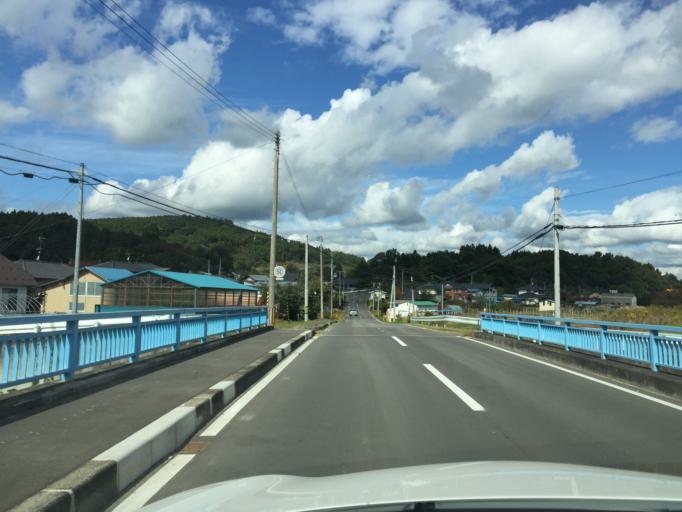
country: JP
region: Fukushima
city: Funehikimachi-funehiki
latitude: 37.4341
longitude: 140.5520
